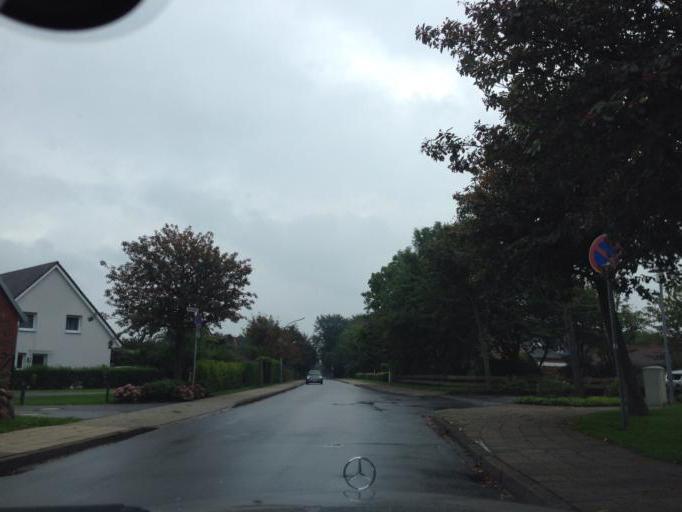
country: DE
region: Schleswig-Holstein
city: Wyk auf Fohr
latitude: 54.6907
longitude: 8.5592
